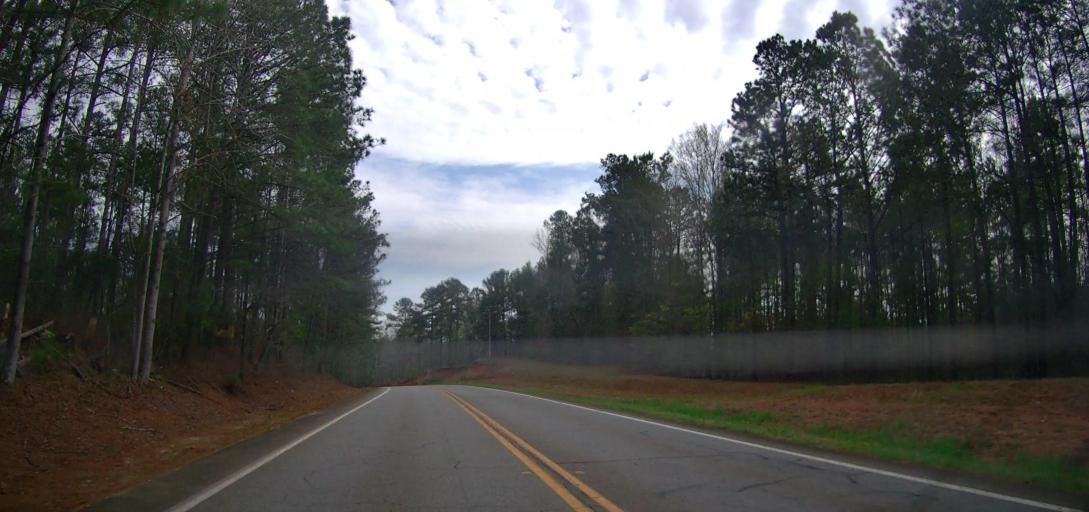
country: US
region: Georgia
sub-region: Jones County
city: Gray
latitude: 32.9905
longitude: -83.6851
